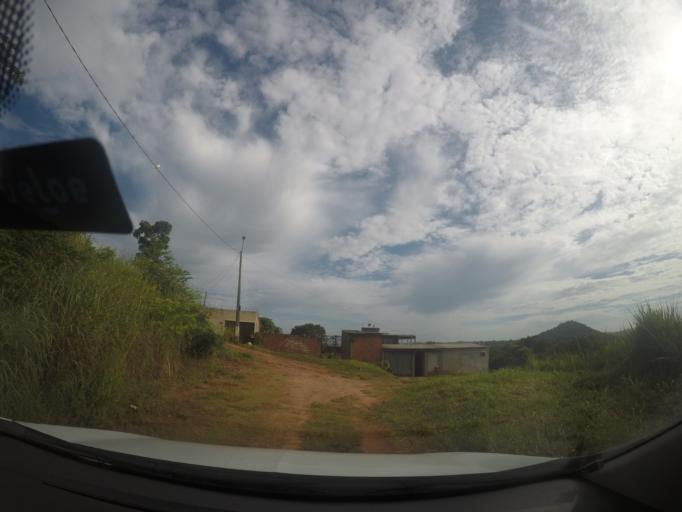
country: BR
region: Goias
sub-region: Goiania
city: Goiania
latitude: -16.6922
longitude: -49.1993
